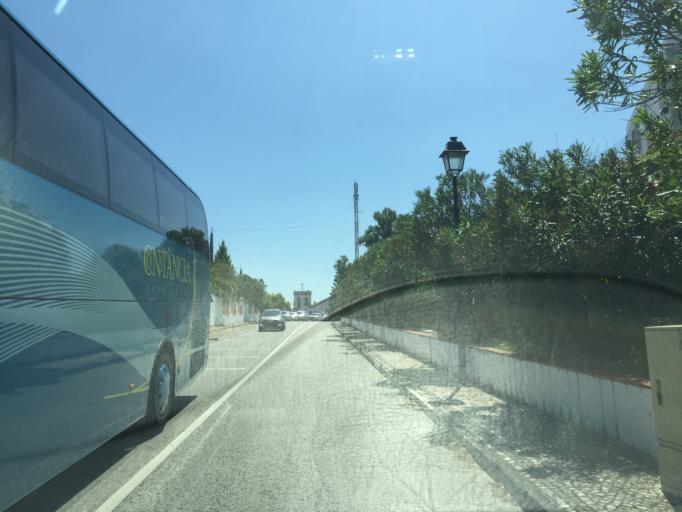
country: PT
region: Santarem
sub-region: Constancia
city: Constancia
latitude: 39.4789
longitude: -8.3352
